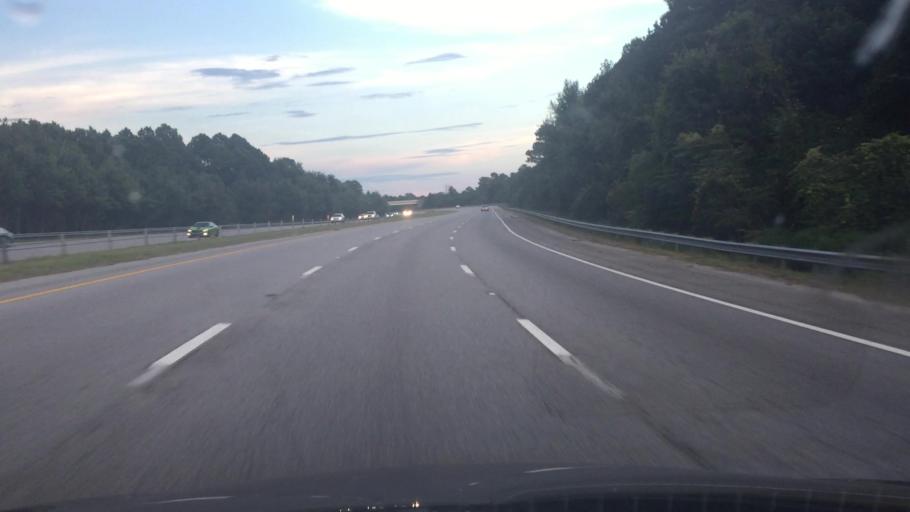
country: US
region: South Carolina
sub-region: Horry County
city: North Myrtle Beach
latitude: 33.8253
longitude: -78.7315
